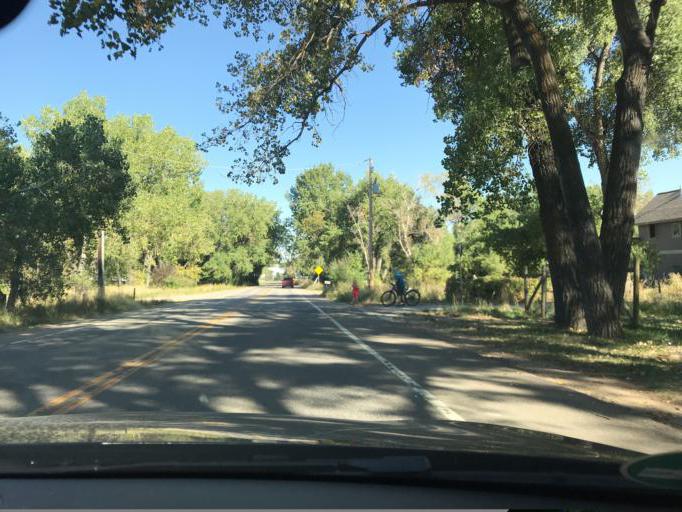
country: US
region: Colorado
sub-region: Boulder County
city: Boulder
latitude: 40.0546
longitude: -105.2763
